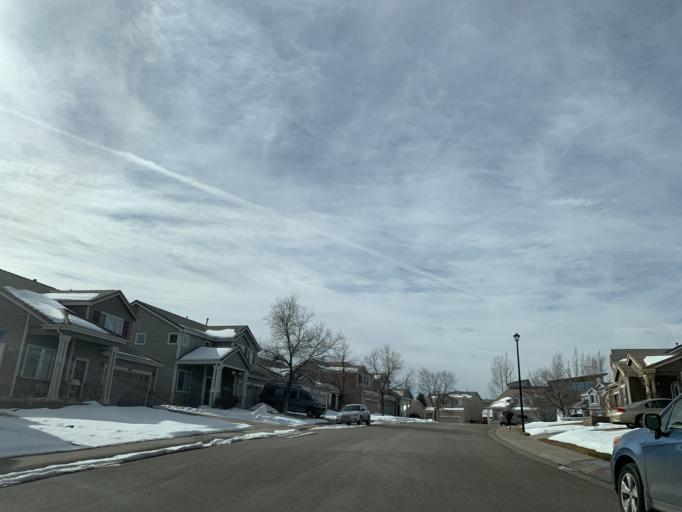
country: US
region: Colorado
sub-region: Douglas County
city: Carriage Club
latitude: 39.5255
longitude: -104.9327
